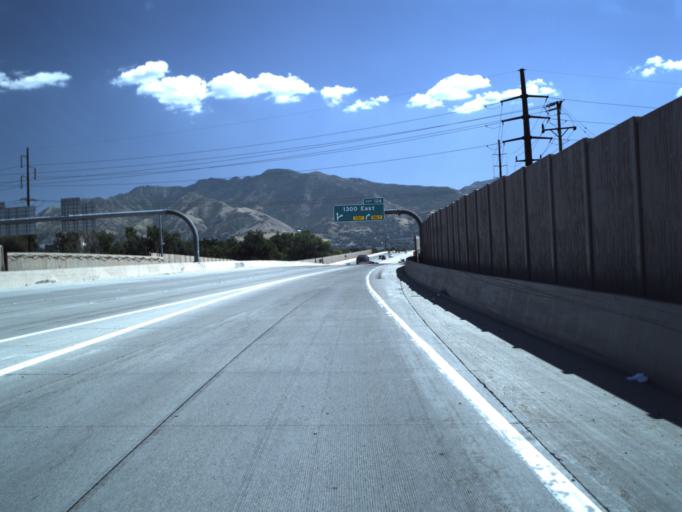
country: US
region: Utah
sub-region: Salt Lake County
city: South Salt Lake
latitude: 40.7191
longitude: -111.8671
